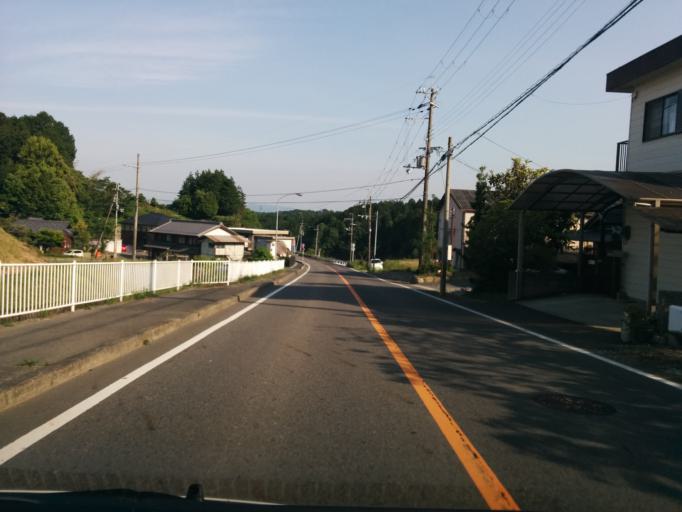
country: JP
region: Shiga Prefecture
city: Kitahama
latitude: 35.1038
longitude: 135.8809
